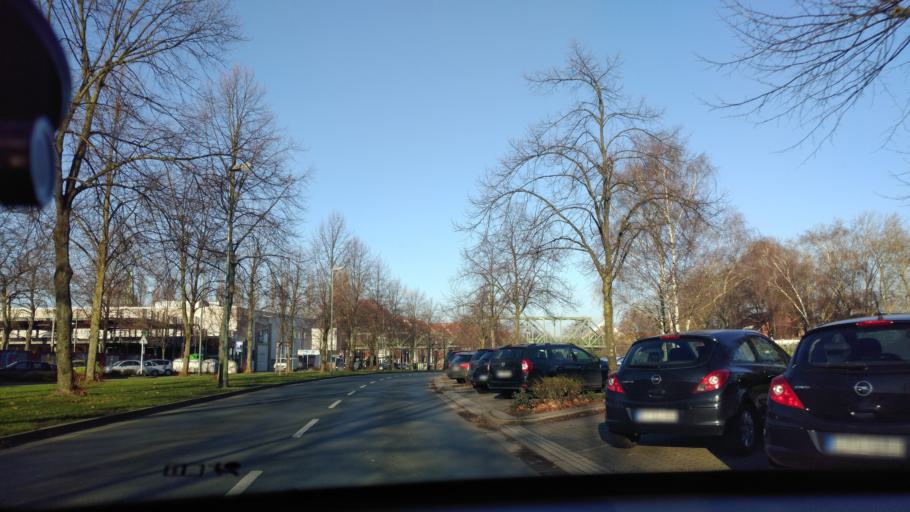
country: DE
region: North Rhine-Westphalia
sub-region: Regierungsbezirk Dusseldorf
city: Essen
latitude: 51.4952
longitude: 7.0105
